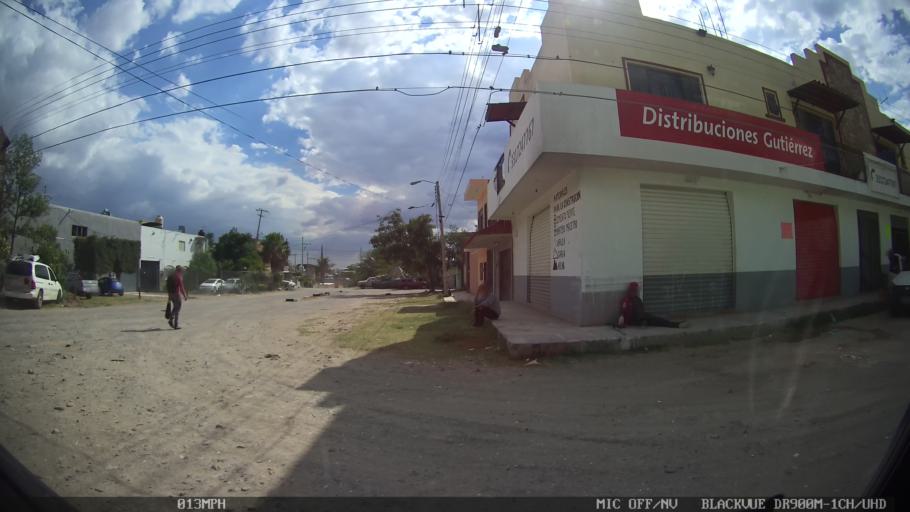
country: MX
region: Jalisco
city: Tlaquepaque
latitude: 20.6605
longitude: -103.2659
